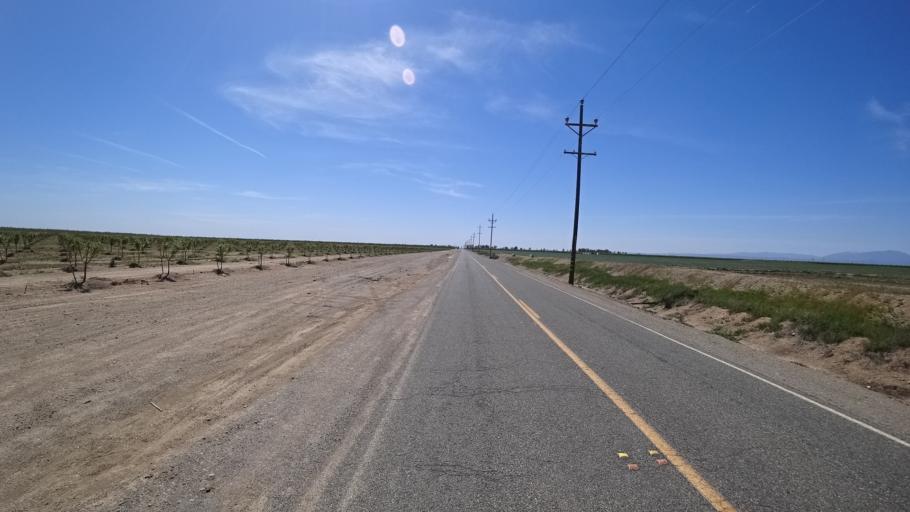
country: US
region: California
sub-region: Glenn County
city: Orland
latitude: 39.6838
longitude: -122.1779
